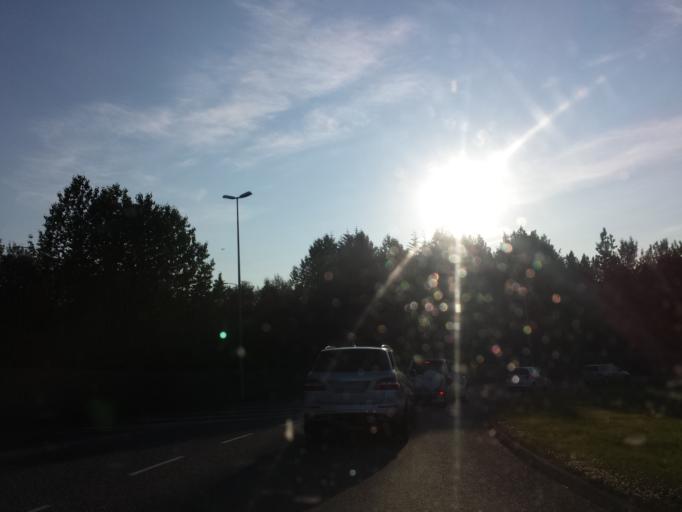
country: IS
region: Capital Region
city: Reykjavik
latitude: 64.1268
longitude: -21.8644
